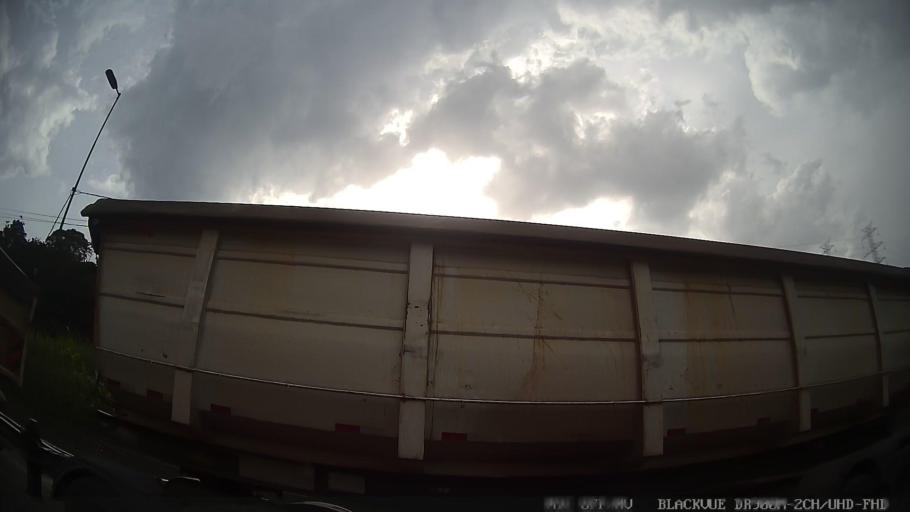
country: BR
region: Sao Paulo
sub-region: Cubatao
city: Cubatao
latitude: -23.8500
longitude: -46.4034
